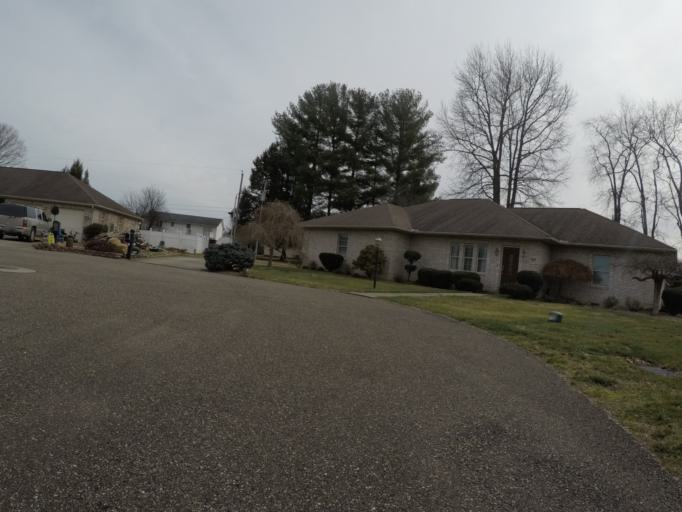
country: US
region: West Virginia
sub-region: Cabell County
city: Pea Ridge
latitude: 38.4498
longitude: -82.3402
